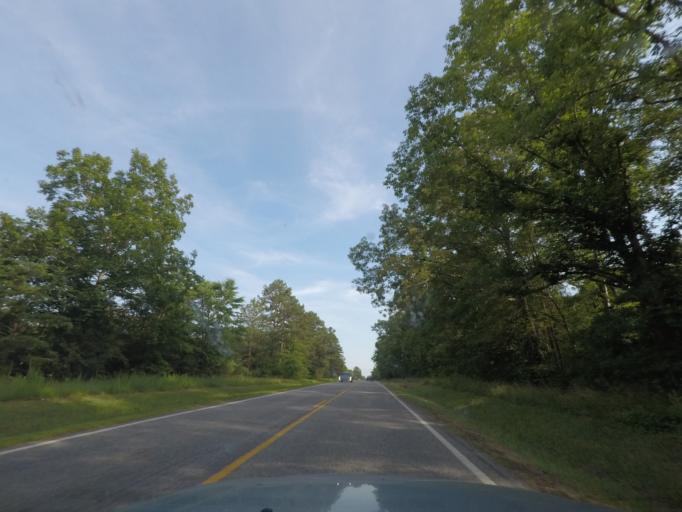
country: US
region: Virginia
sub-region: Mecklenburg County
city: Clarksville
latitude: 36.5478
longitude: -78.5402
